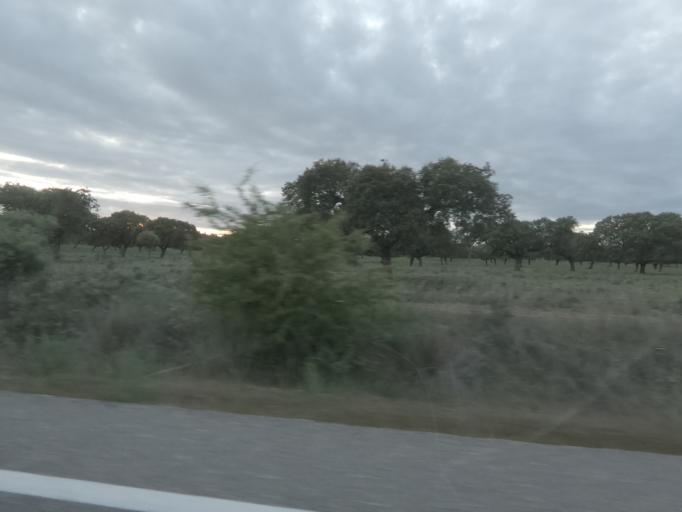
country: ES
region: Extremadura
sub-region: Provincia de Badajoz
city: La Roca de la Sierra
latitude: 39.0745
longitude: -6.7510
